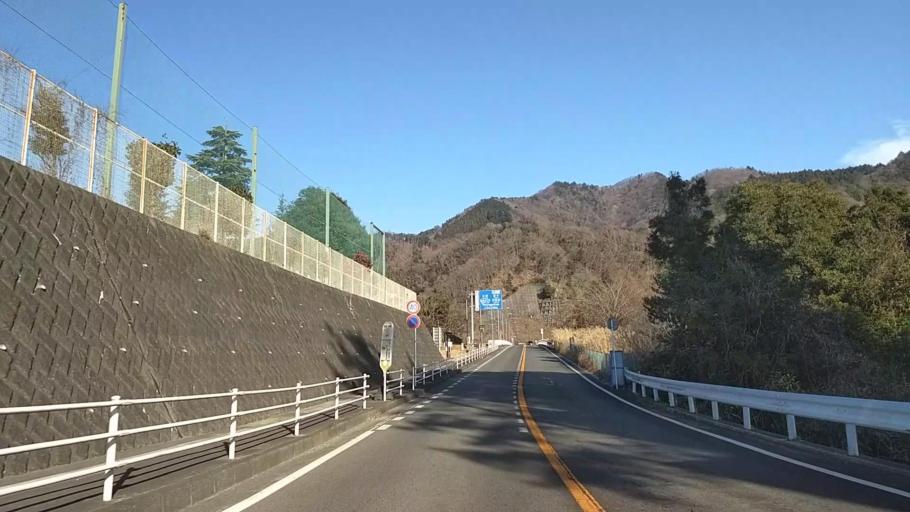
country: JP
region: Yamanashi
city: Uenohara
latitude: 35.5232
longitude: 139.2317
